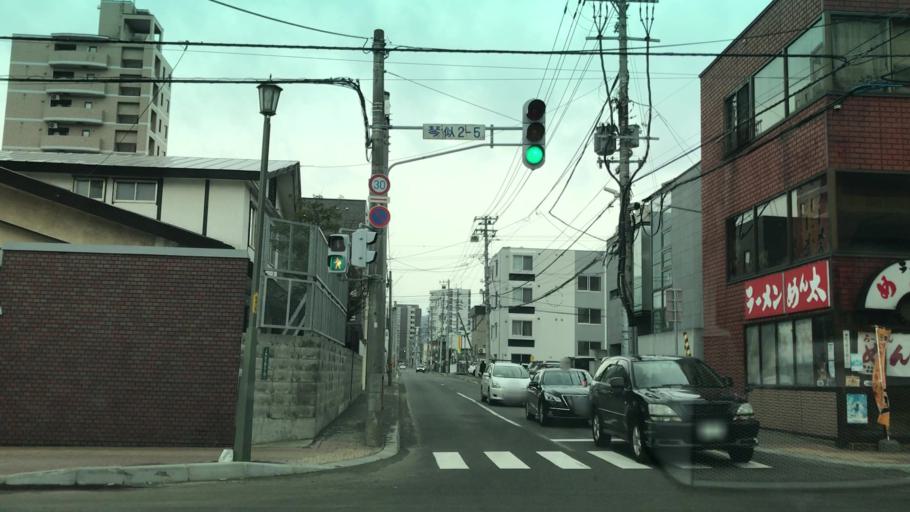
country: JP
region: Hokkaido
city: Sapporo
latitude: 43.0773
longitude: 141.3012
